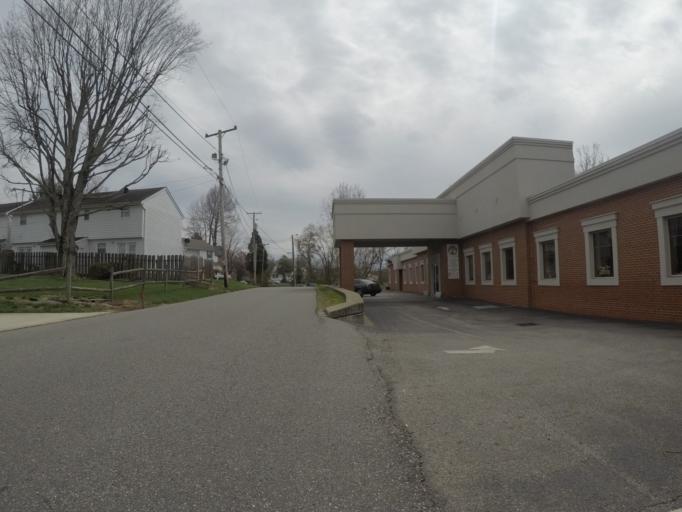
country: US
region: West Virginia
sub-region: Cabell County
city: Pea Ridge
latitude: 38.4174
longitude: -82.3218
